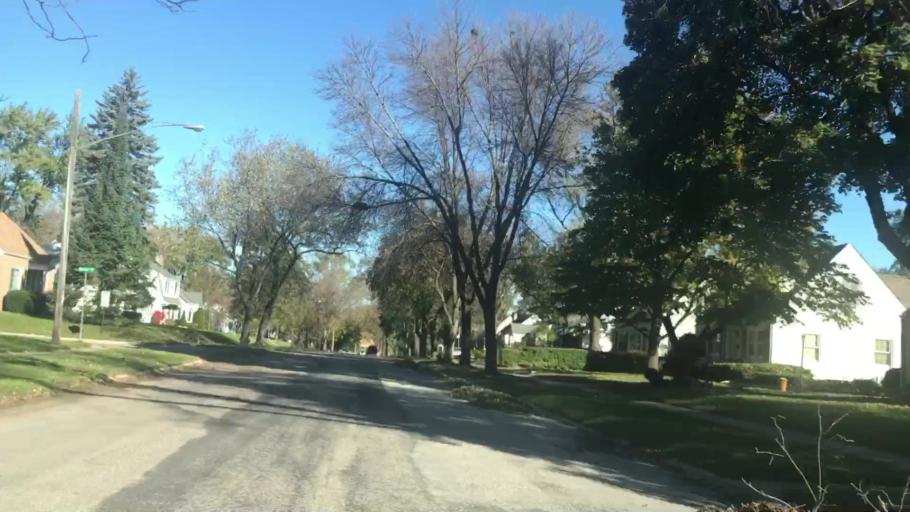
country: US
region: Wisconsin
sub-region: Waukesha County
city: Menomonee Falls
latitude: 43.1722
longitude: -88.1144
